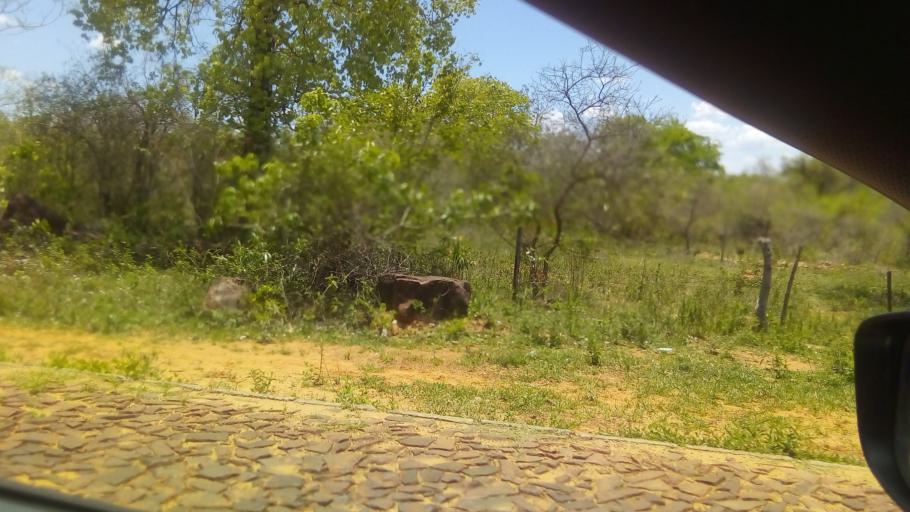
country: PY
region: Cordillera
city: Arroyos y Esteros
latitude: -24.9865
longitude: -57.2062
